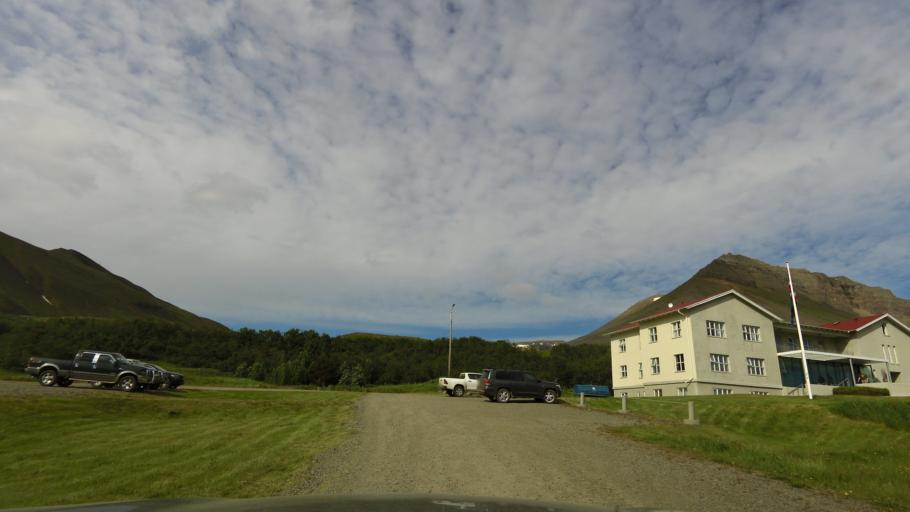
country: IS
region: Westfjords
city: Isafjoerdur
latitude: 65.7595
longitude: -23.4521
